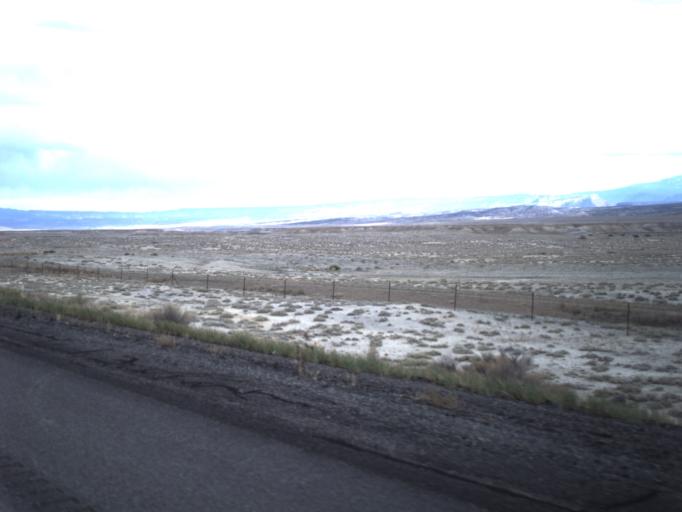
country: US
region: Utah
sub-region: Grand County
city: Moab
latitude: 38.9332
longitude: -109.4472
